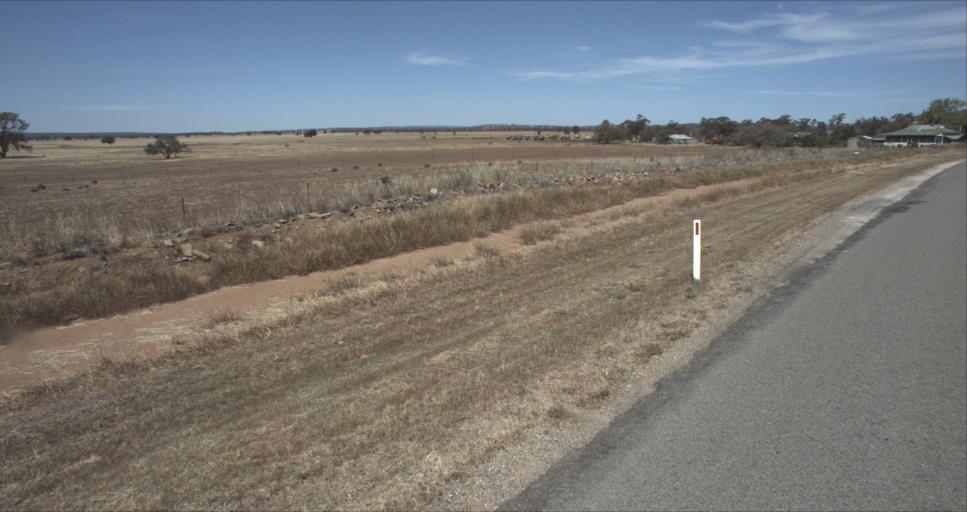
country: AU
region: New South Wales
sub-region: Leeton
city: Leeton
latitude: -34.6003
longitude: 146.4794
